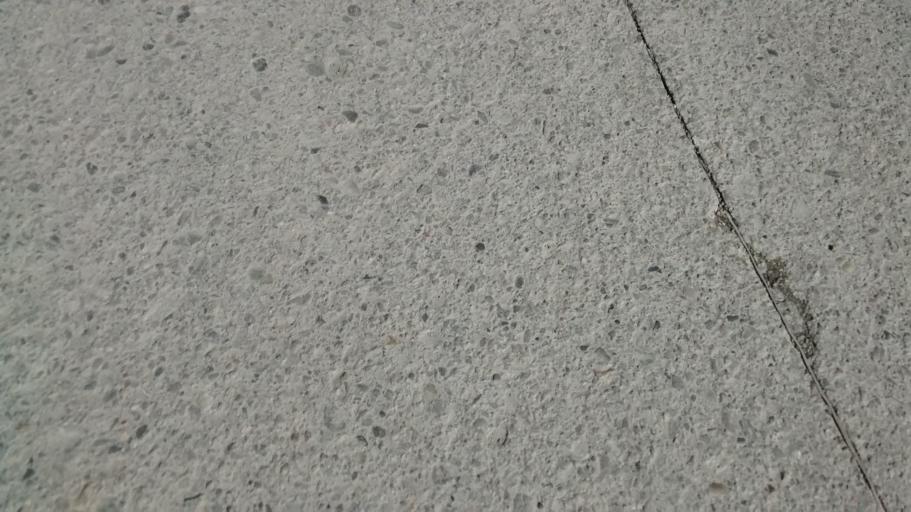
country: AR
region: Tierra del Fuego
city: Ushuaia
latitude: -54.8035
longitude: -68.2992
